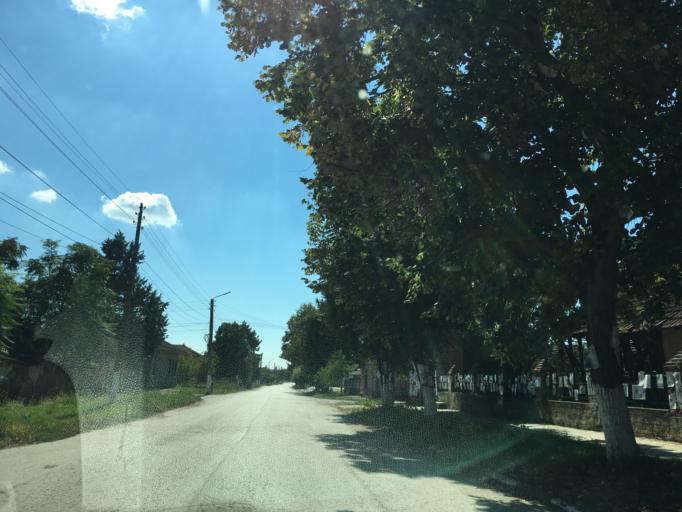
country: RO
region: Olt
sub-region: Comuna Orlea
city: Orlea
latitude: 43.6472
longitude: 24.4006
